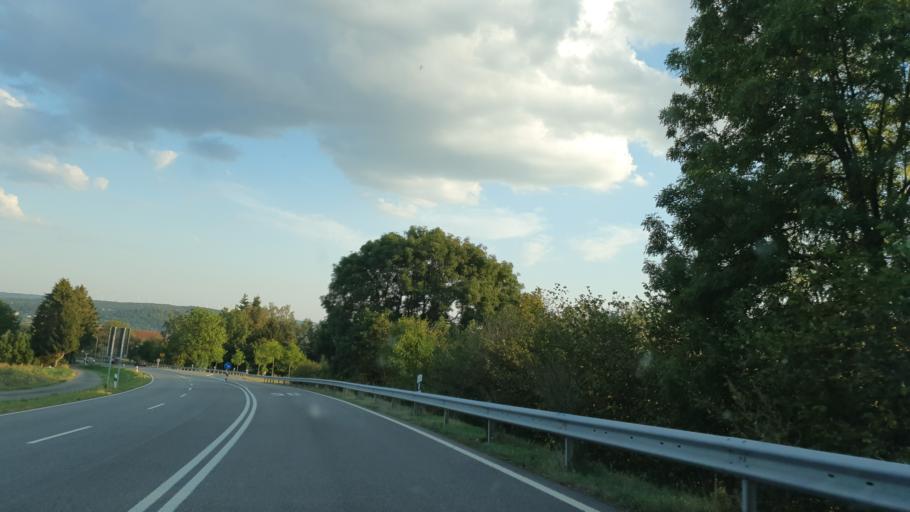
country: DE
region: Rheinland-Pfalz
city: Ellenberg
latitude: 49.6611
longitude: 7.1449
